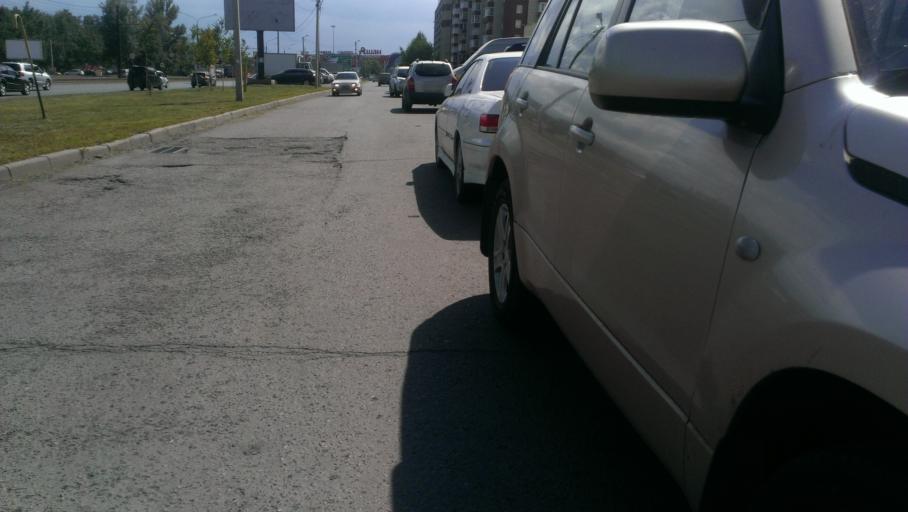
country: RU
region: Altai Krai
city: Novosilikatnyy
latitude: 53.3326
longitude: 83.6926
